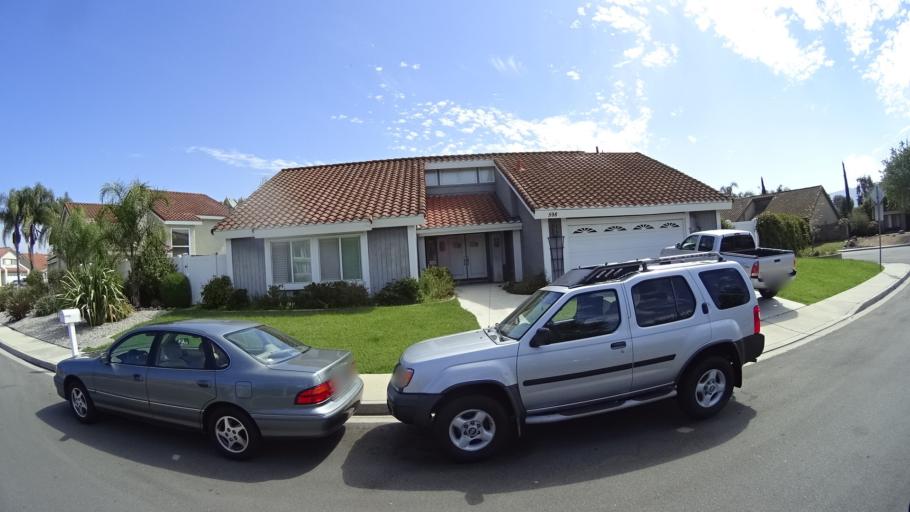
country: US
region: California
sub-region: Ventura County
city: Casa Conejo
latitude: 34.1863
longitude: -118.9381
